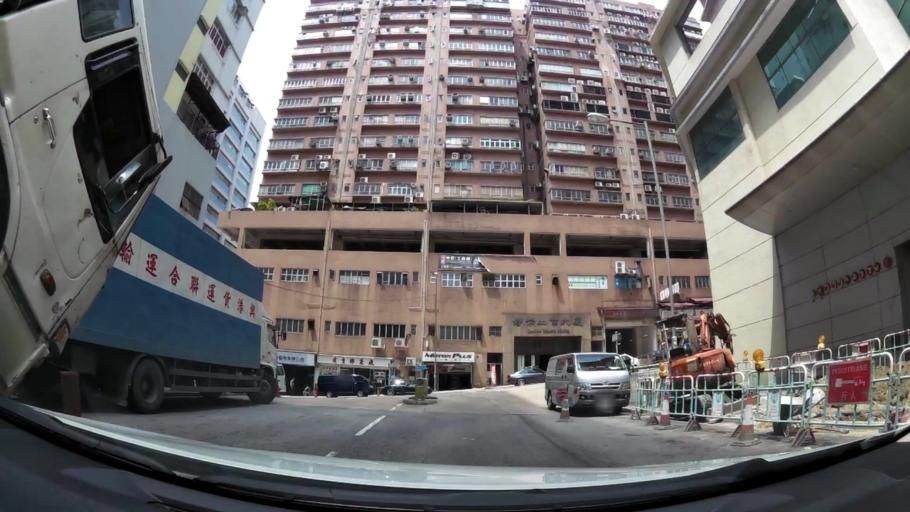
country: HK
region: Tuen Mun
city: Tuen Mun
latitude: 22.3983
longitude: 113.9683
